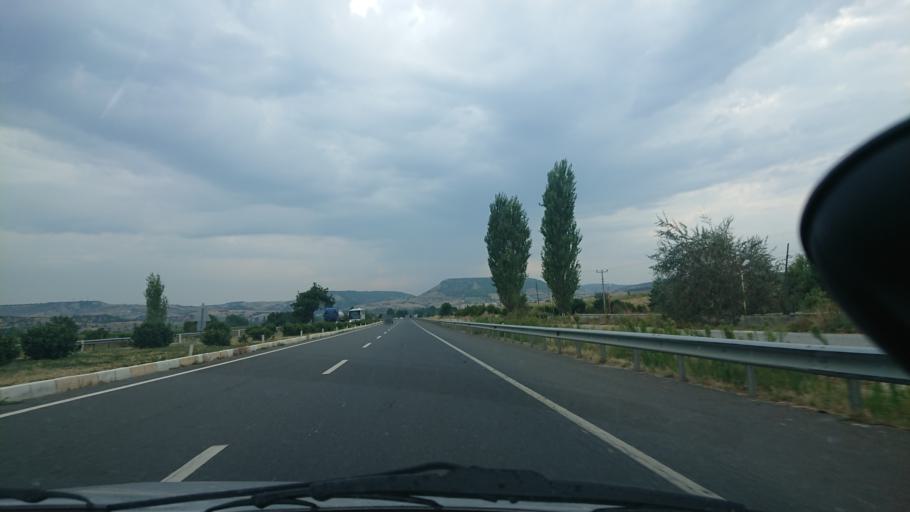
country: TR
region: Manisa
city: Selendi
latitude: 38.6184
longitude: 28.8990
